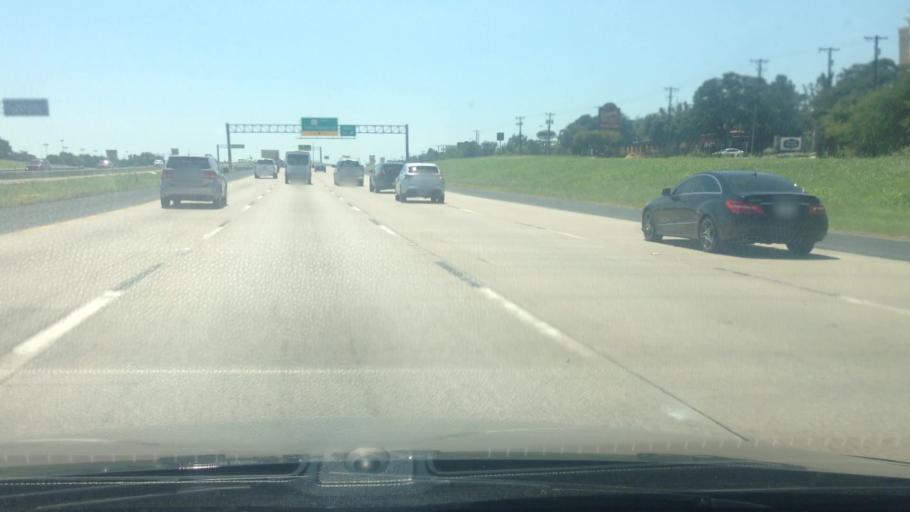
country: US
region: Texas
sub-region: Tarrant County
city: Grapevine
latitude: 32.8878
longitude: -97.0994
